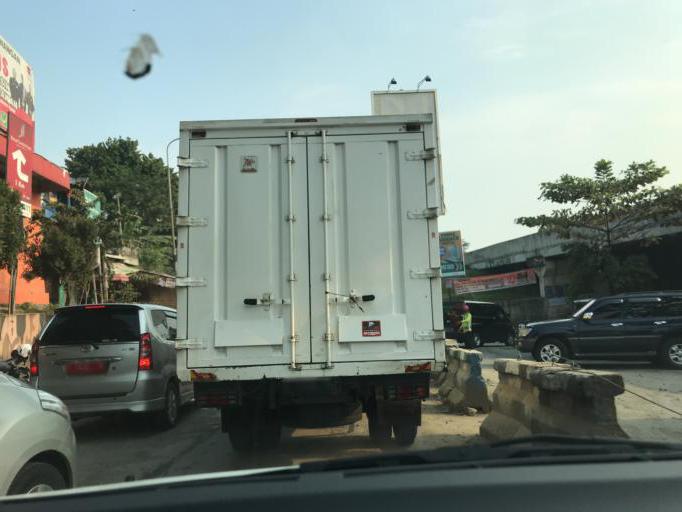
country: ID
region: West Java
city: Cibinong
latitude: -6.5325
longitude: 106.8530
